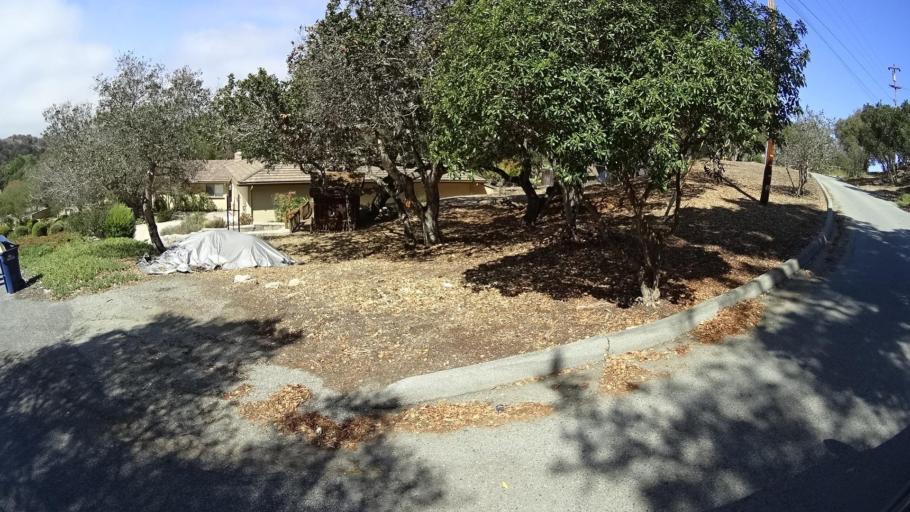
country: US
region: California
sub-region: Monterey County
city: Carmel Valley Village
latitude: 36.5679
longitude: -121.7529
